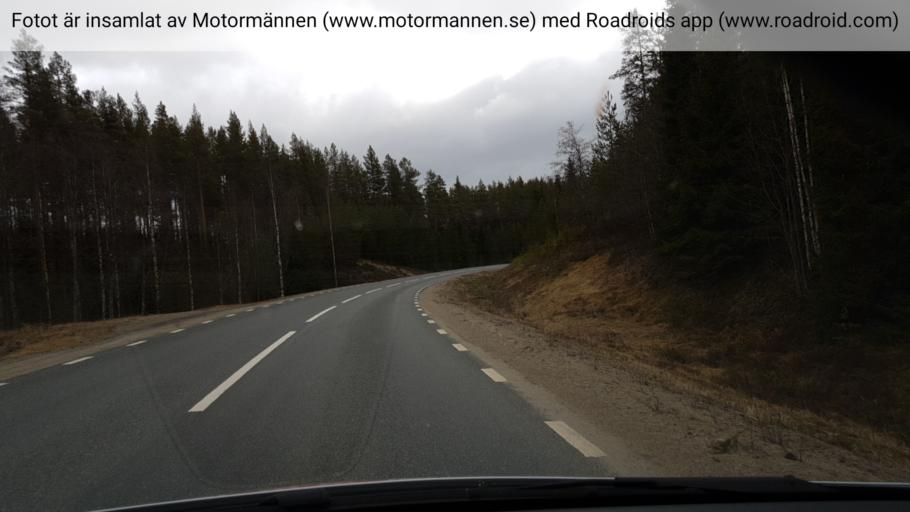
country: SE
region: Vaesternorrland
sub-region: OErnskoeldsviks Kommun
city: Bredbyn
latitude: 63.8010
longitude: 18.4952
